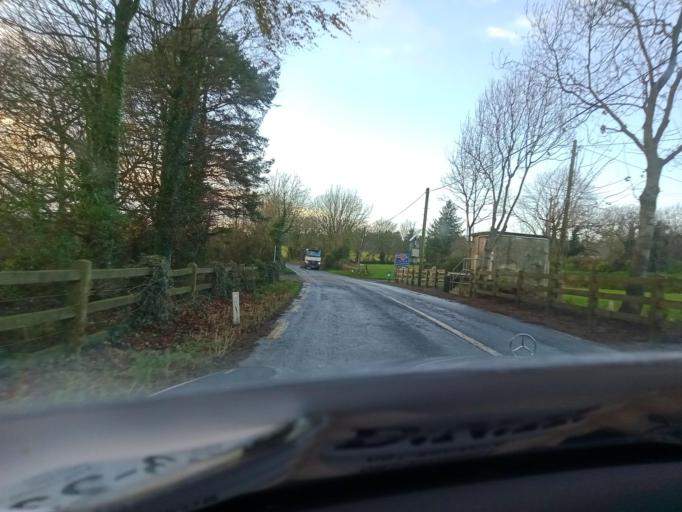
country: IE
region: Munster
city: Carrick-on-Suir
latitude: 52.3317
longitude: -7.4074
